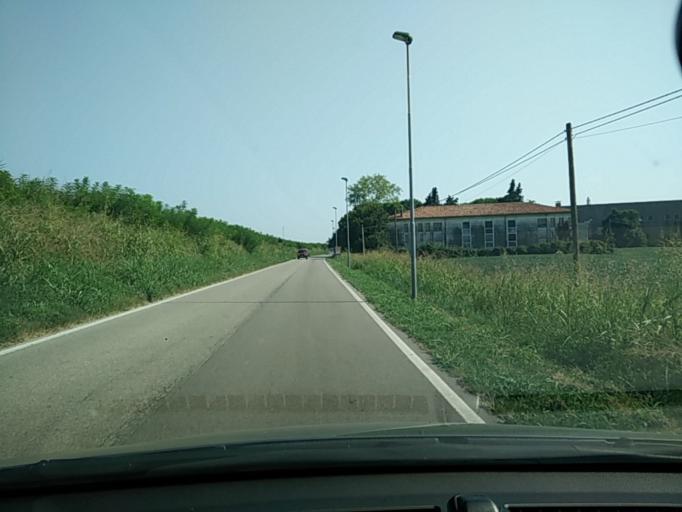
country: IT
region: Veneto
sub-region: Provincia di Venezia
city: Caorle
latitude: 45.6160
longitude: 12.8600
